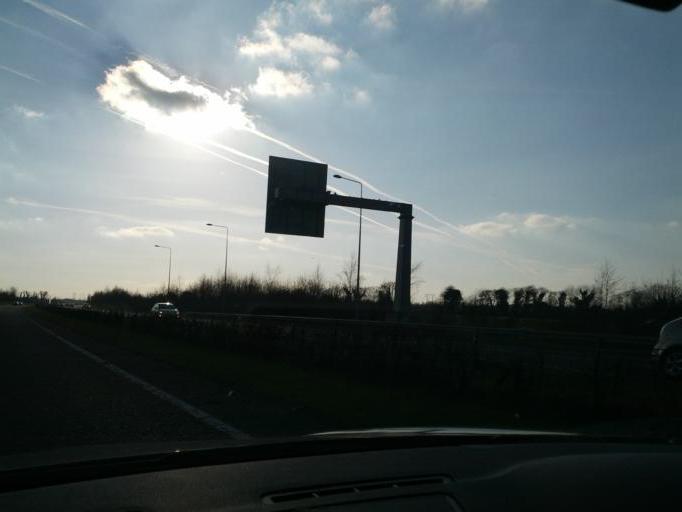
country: IE
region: Leinster
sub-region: Laois
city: Stradbally
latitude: 53.0857
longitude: -7.1787
